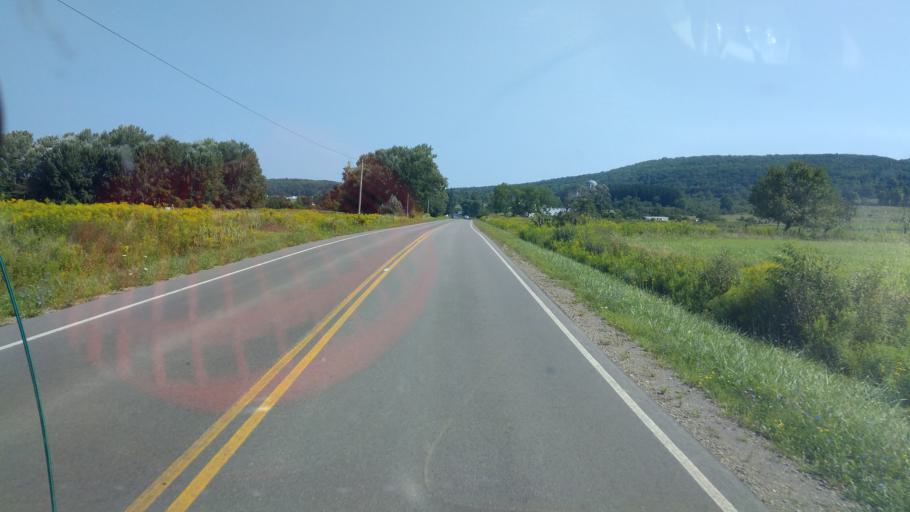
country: US
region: New York
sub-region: Allegany County
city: Belmont
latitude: 42.2773
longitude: -78.0364
